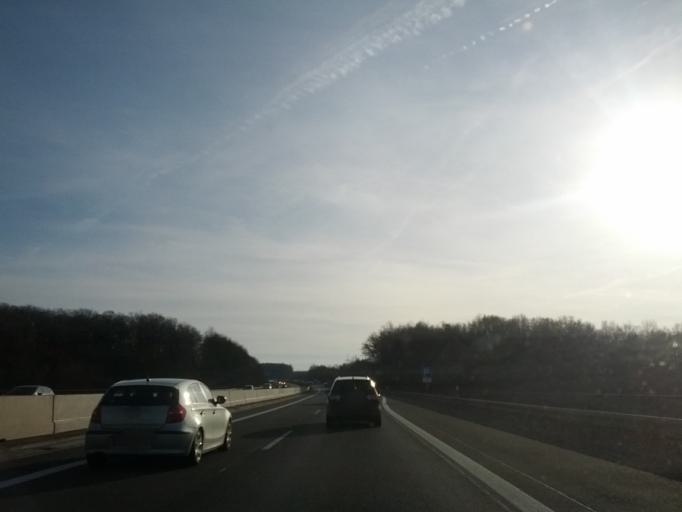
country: DE
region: Bavaria
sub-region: Regierungsbezirk Unterfranken
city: Rottendorf
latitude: 49.8026
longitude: 10.0474
